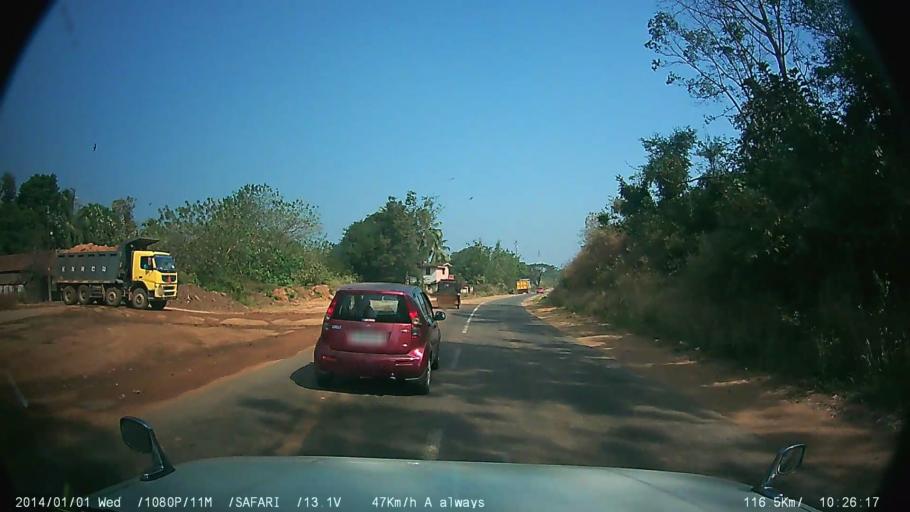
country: IN
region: Kerala
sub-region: Thrissur District
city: Chelakara
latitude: 10.6258
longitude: 76.5121
